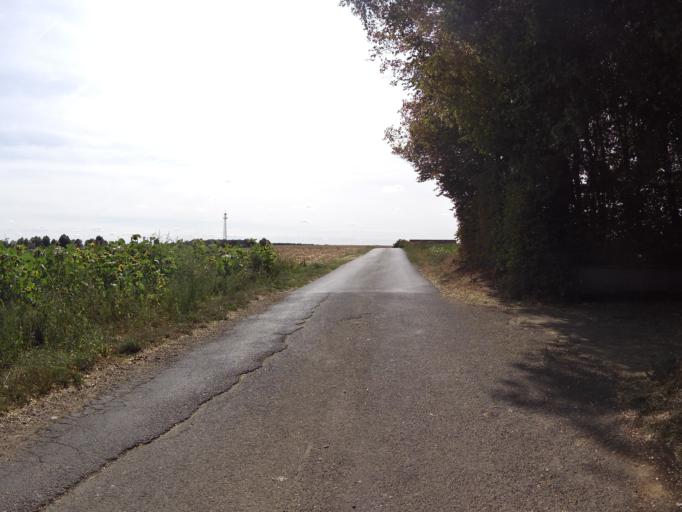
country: DE
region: Bavaria
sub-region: Regierungsbezirk Unterfranken
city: Rimpar
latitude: 49.8466
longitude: 9.9386
